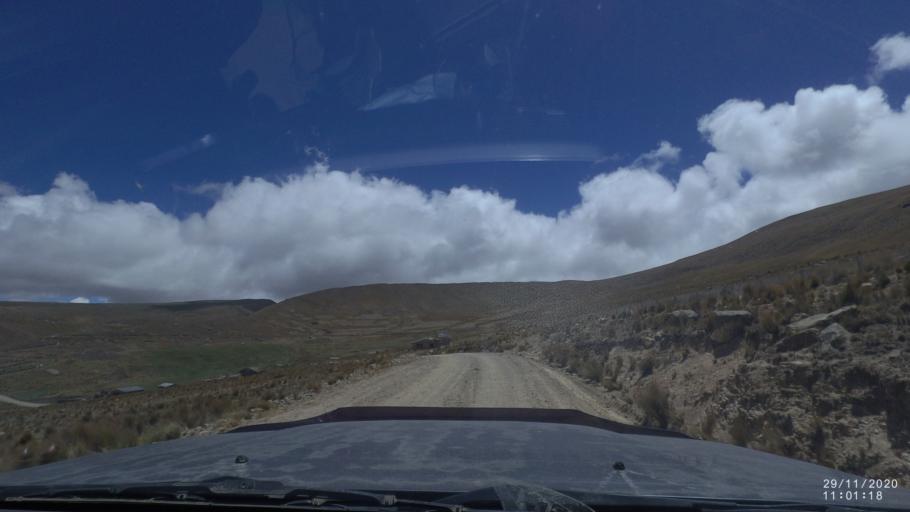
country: BO
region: Cochabamba
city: Cochabamba
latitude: -17.1990
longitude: -66.2244
